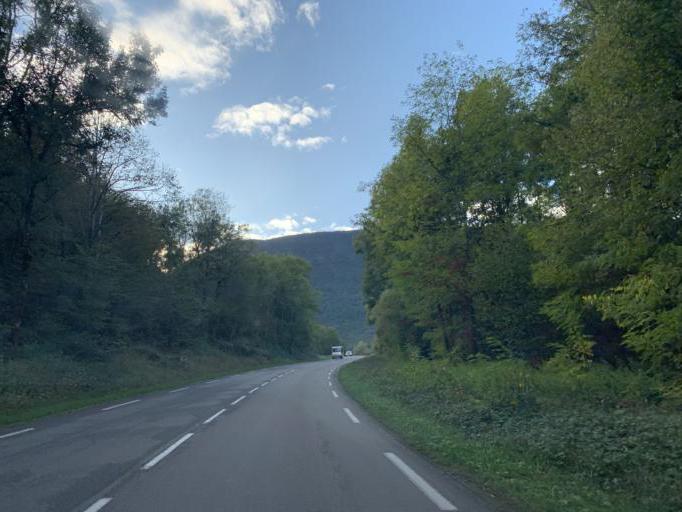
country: FR
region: Rhone-Alpes
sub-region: Departement de l'Ain
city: Artemare
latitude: 45.8631
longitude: 5.6723
